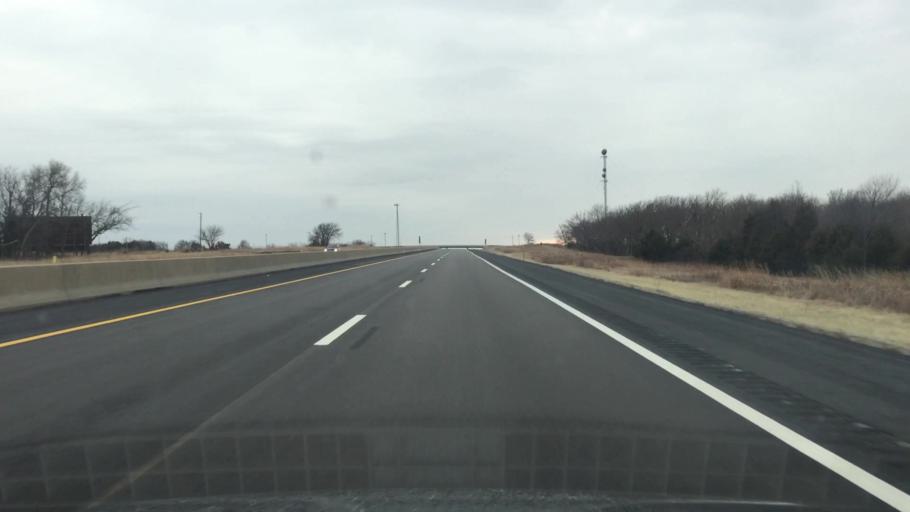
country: US
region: Kansas
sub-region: Shawnee County
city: Auburn
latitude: 38.8457
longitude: -95.8664
